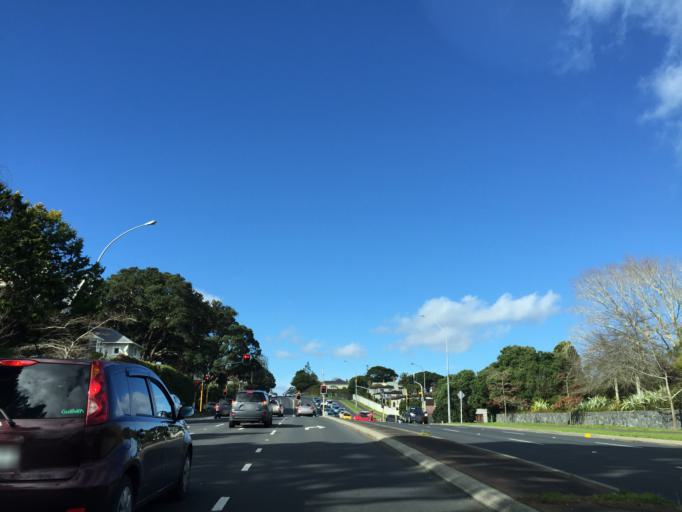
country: NZ
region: Auckland
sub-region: Auckland
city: Auckland
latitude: -36.8896
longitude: 174.7589
